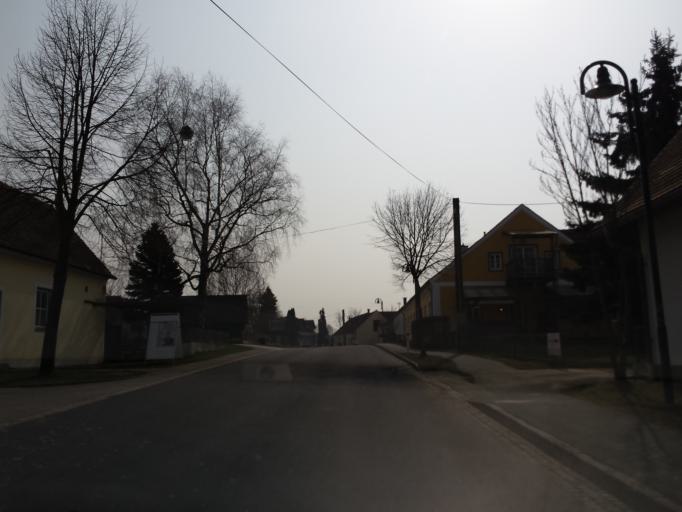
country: AT
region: Styria
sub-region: Politischer Bezirk Hartberg-Fuerstenfeld
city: Loipersdorf bei Fuerstenfeld
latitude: 47.0184
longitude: 16.1041
